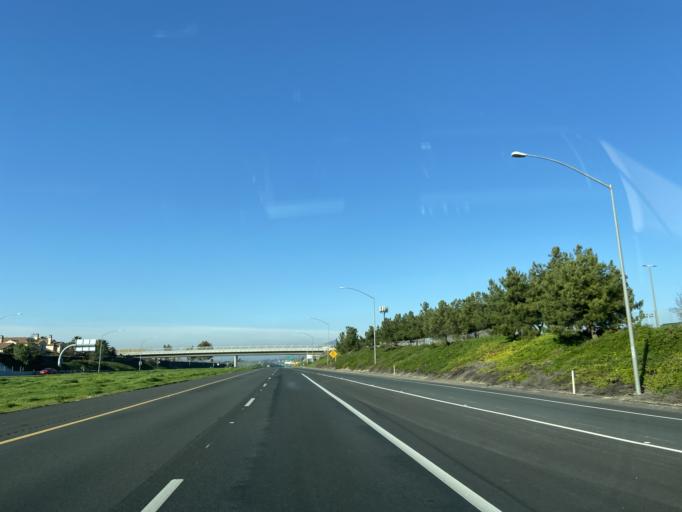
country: US
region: California
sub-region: San Diego County
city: Bonita
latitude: 32.6234
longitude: -116.9712
